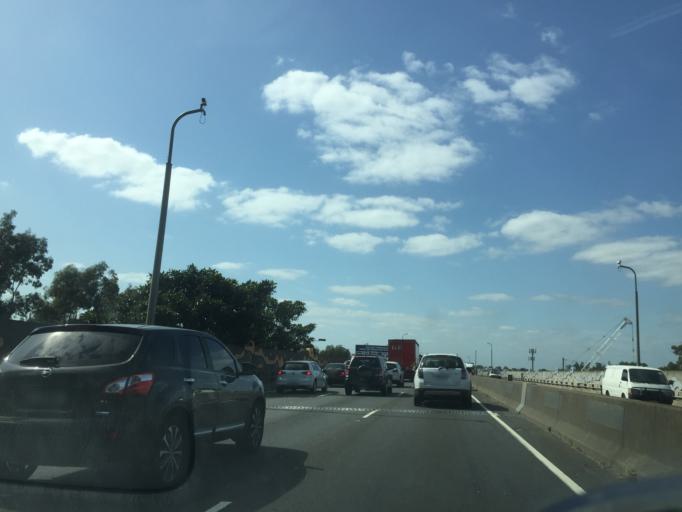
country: AU
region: New South Wales
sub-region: Parramatta
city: Granville
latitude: -33.8294
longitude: 151.0181
